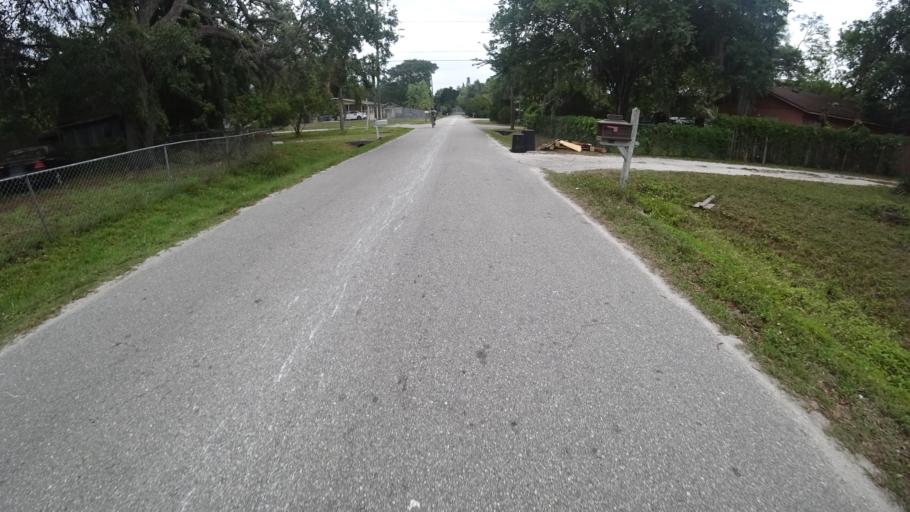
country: US
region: Florida
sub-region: Manatee County
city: Samoset
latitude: 27.4713
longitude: -82.5428
